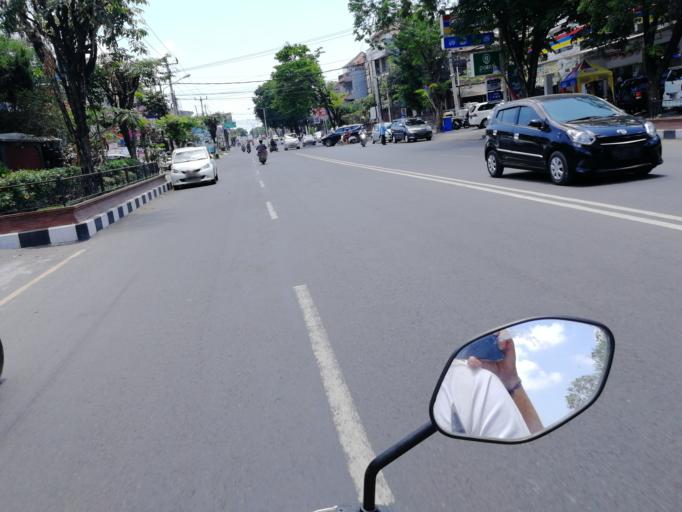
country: ID
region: Bali
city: Banjar Kertasari
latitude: -8.6369
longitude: 115.1821
